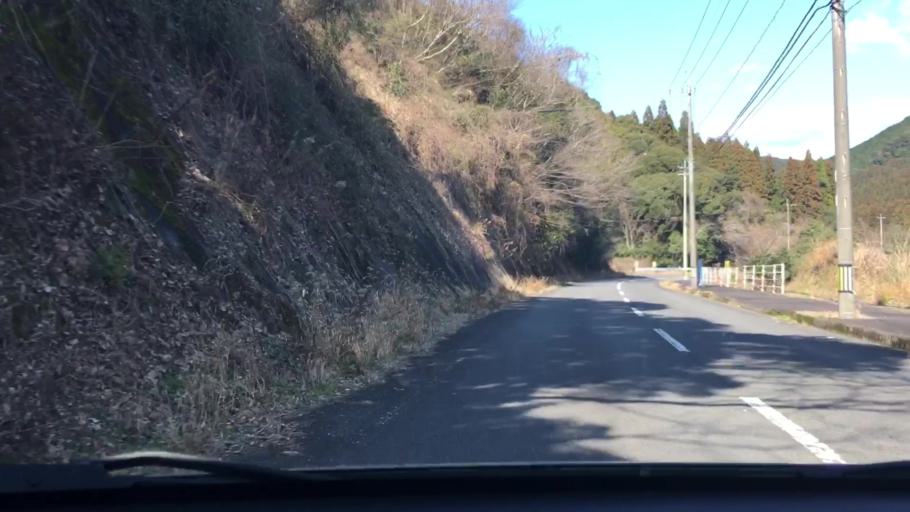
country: JP
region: Kagoshima
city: Ijuin
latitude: 31.7455
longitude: 130.4091
